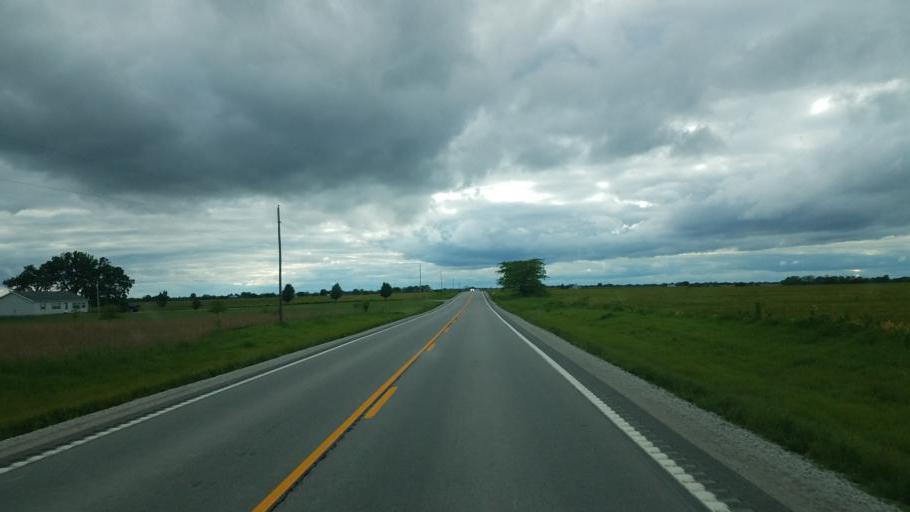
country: US
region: Missouri
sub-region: Harrison County
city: Bethany
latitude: 40.2769
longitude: -93.8385
